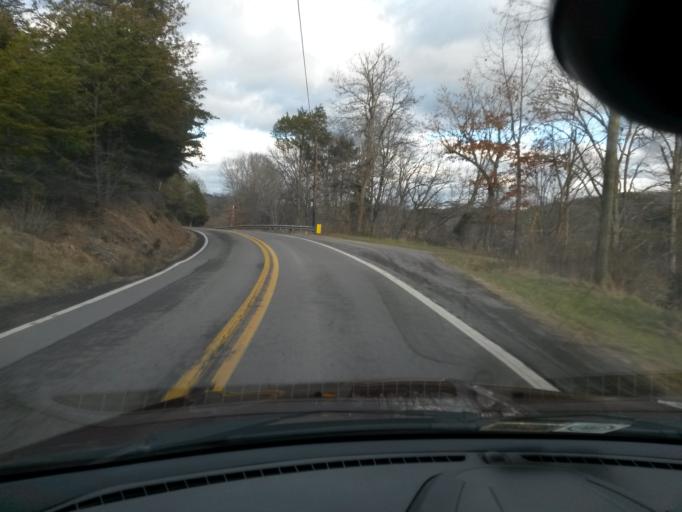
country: US
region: West Virginia
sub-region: Monroe County
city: Union
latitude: 37.5418
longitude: -80.5950
